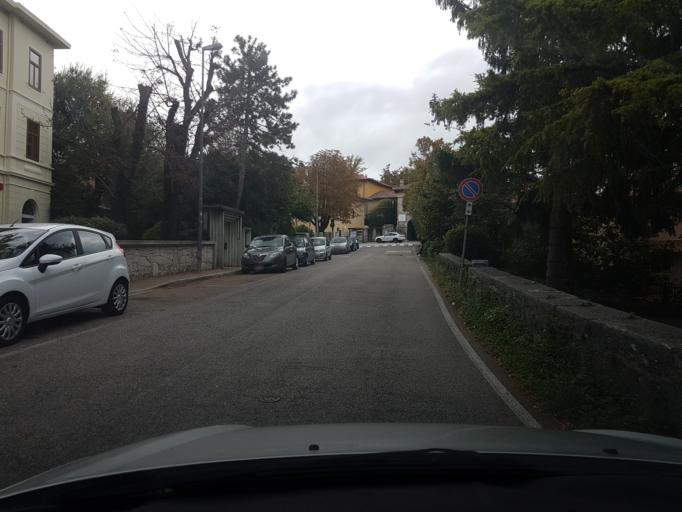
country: IT
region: Friuli Venezia Giulia
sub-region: Provincia di Trieste
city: Duino
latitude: 45.7741
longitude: 13.6043
